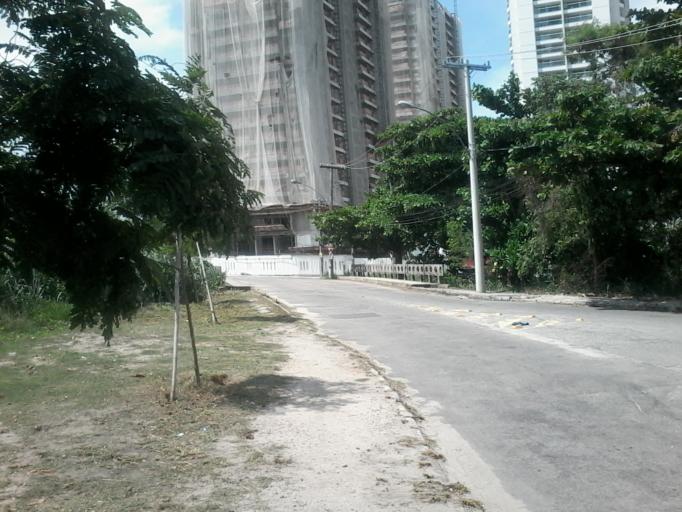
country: BR
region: Rio de Janeiro
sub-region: Nilopolis
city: Nilopolis
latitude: -23.0227
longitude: -43.4913
